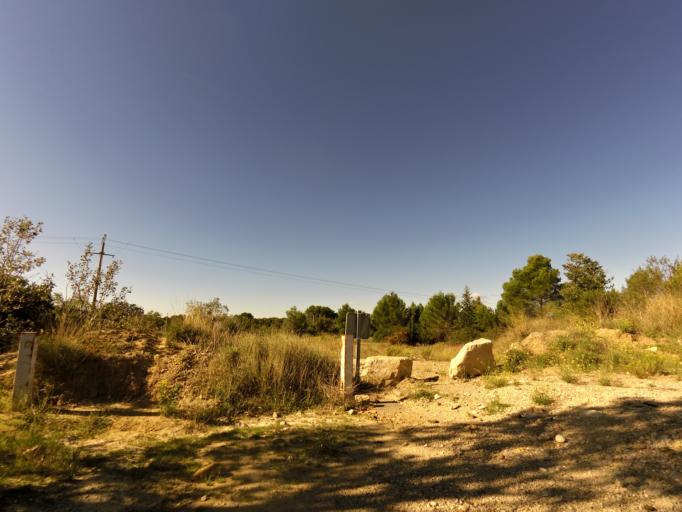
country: FR
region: Languedoc-Roussillon
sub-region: Departement de l'Herault
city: Villetelle
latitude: 43.7267
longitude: 4.1516
